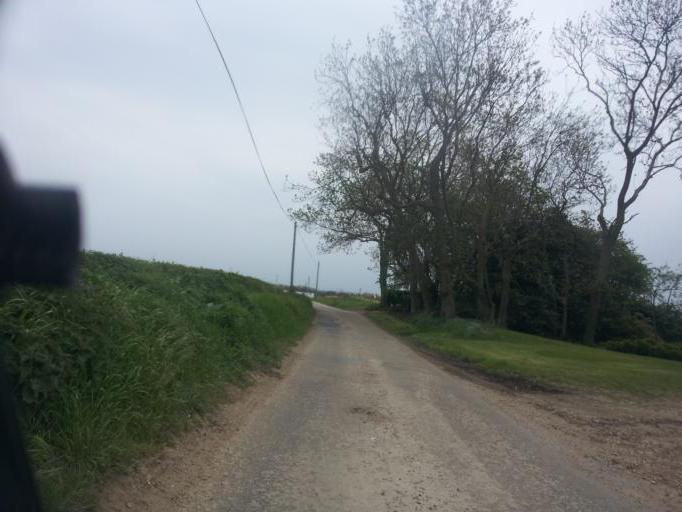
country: GB
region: England
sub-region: Medway
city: Stoke
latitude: 51.4589
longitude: 0.5966
